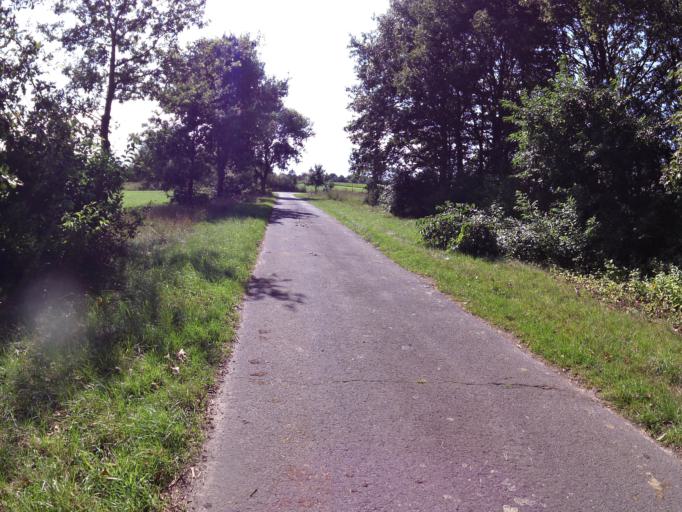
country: DE
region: Lower Saxony
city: Sandbostel
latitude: 53.3889
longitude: 9.1226
